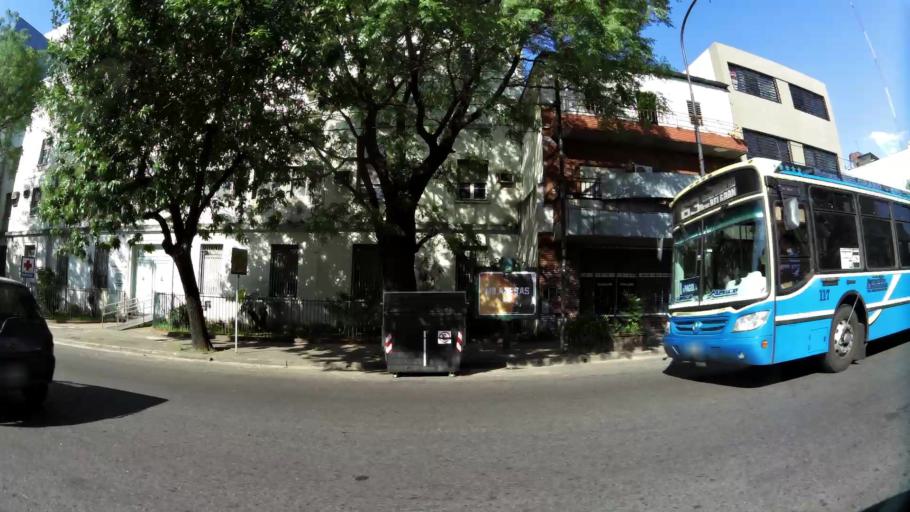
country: AR
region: Buenos Aires F.D.
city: Villa Santa Rita
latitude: -34.6200
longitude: -58.4743
